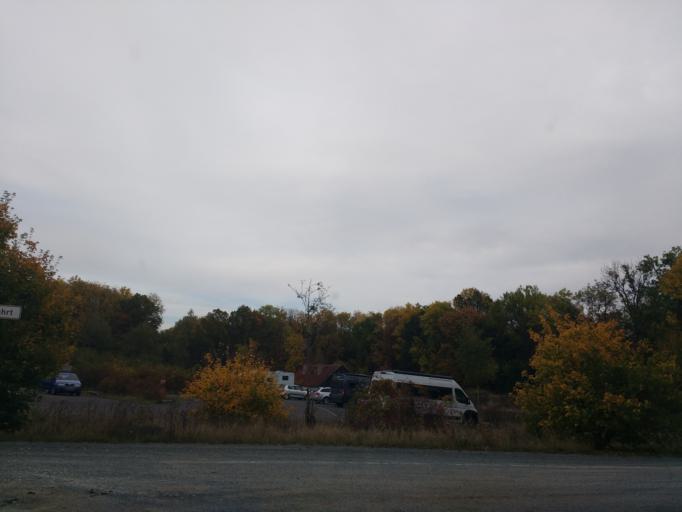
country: DE
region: Thuringia
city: Weberstedt
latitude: 51.0807
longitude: 10.5172
